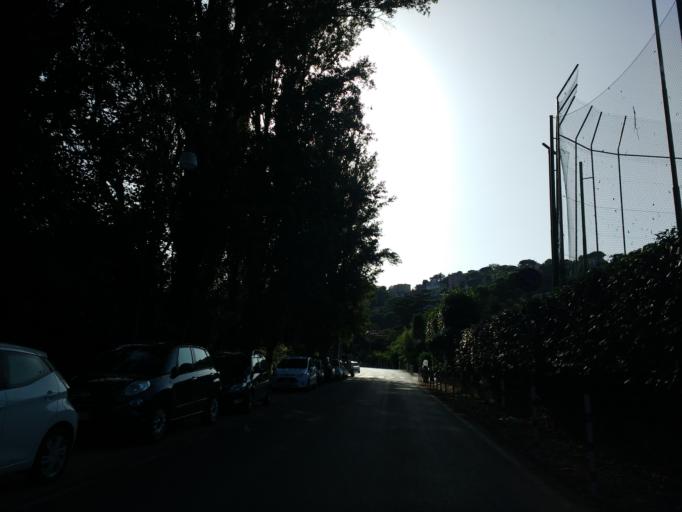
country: IT
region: Latium
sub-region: Citta metropolitana di Roma Capitale
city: Castel Gandolfo
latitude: 41.7615
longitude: 12.6596
